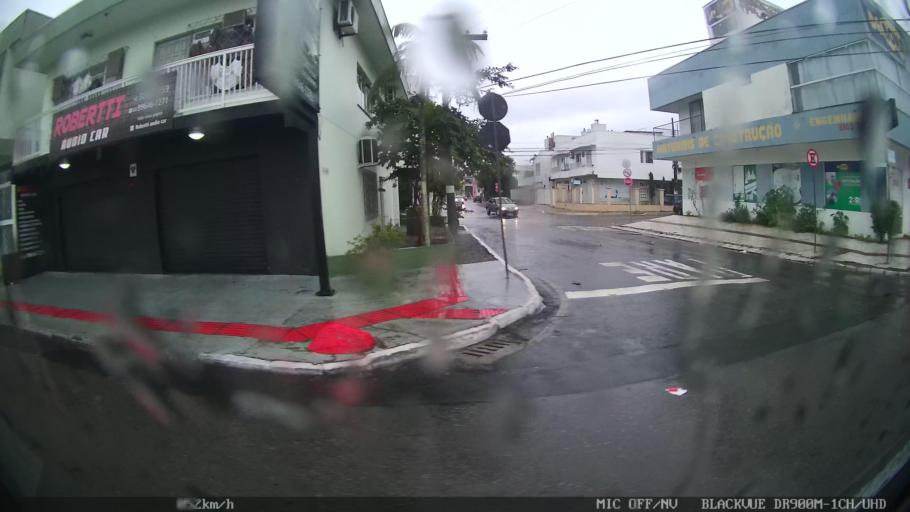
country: BR
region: Santa Catarina
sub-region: Balneario Camboriu
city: Balneario Camboriu
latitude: -26.9954
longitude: -48.6429
